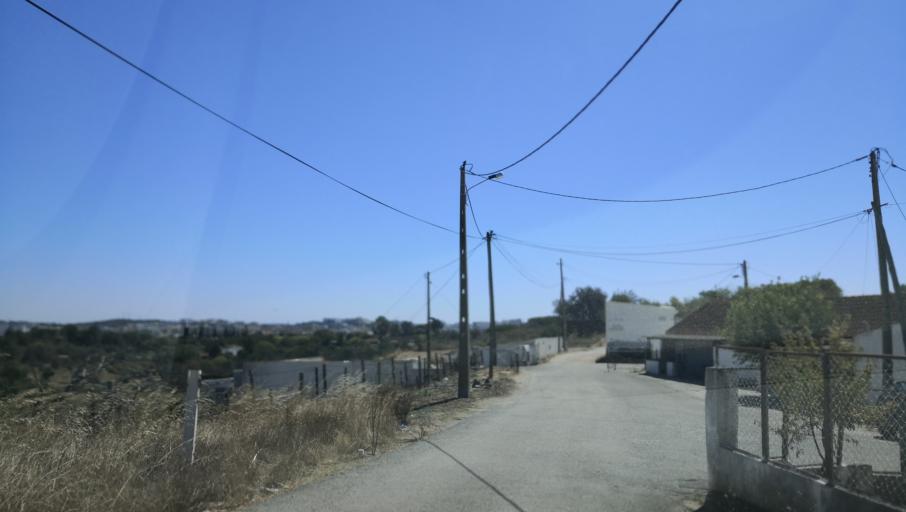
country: PT
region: Setubal
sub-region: Setubal
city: Setubal
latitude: 38.5362
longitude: -8.9122
